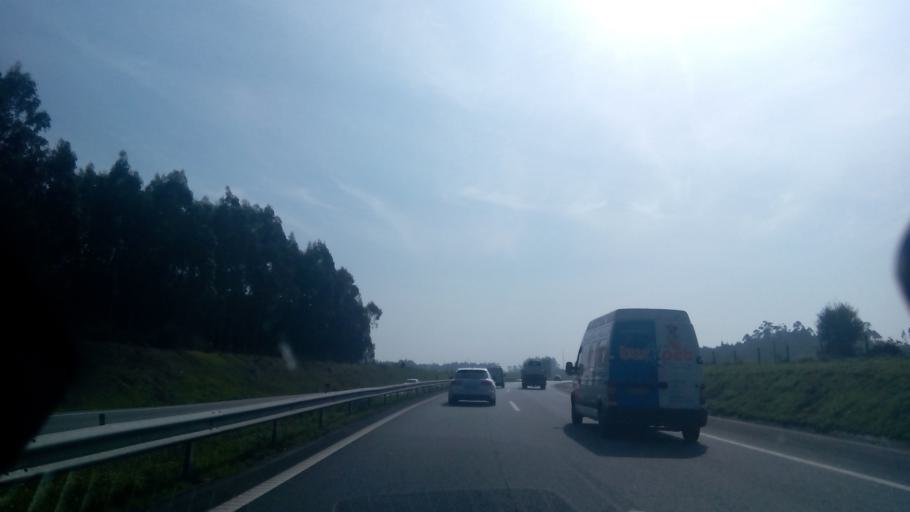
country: PT
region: Porto
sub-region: Vila do Conde
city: Arvore
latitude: 41.3567
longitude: -8.7137
